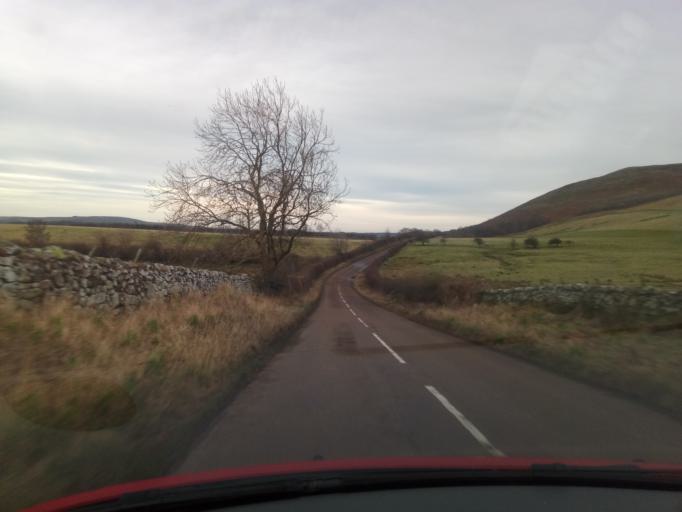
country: GB
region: England
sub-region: Northumberland
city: Kirknewton
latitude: 55.5661
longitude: -2.1009
